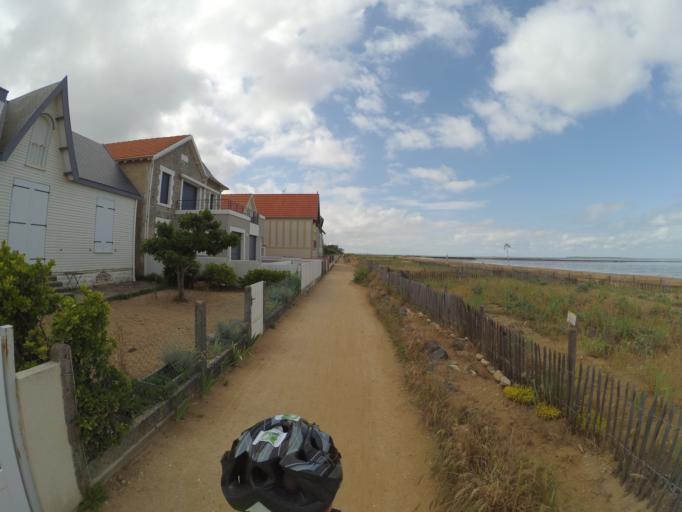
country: FR
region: Poitou-Charentes
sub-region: Departement de la Charente-Maritime
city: Chatelaillon-Plage
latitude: 46.0683
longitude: -1.0929
